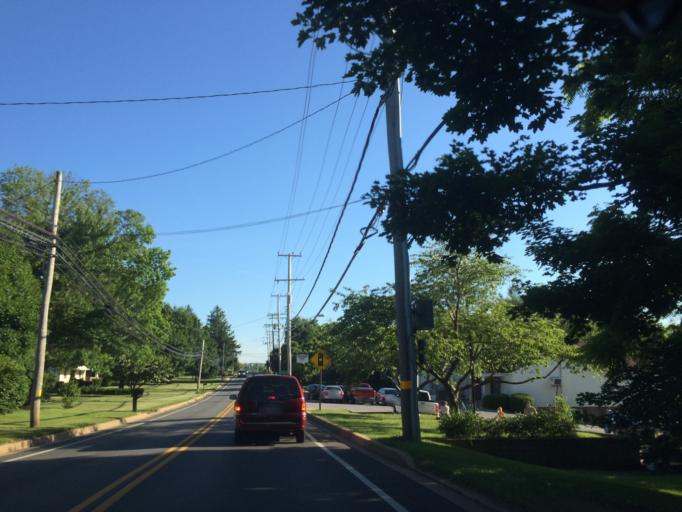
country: US
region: Maryland
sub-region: Carroll County
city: Westminster
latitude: 39.5481
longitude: -76.9920
